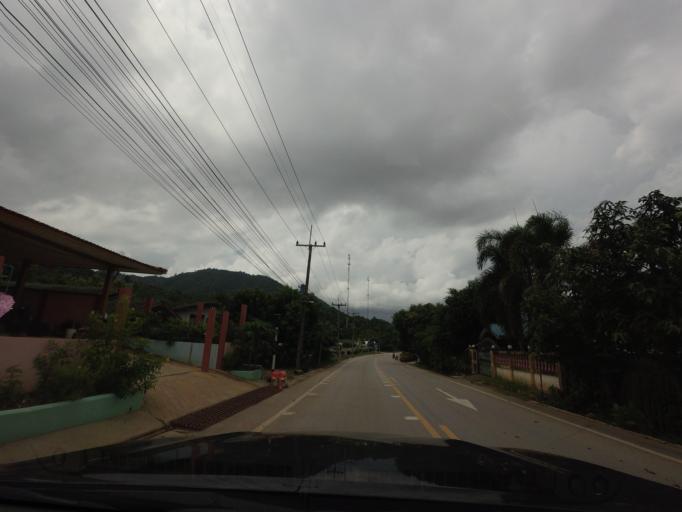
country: TH
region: Loei
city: Pak Chom
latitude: 18.0580
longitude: 101.8014
